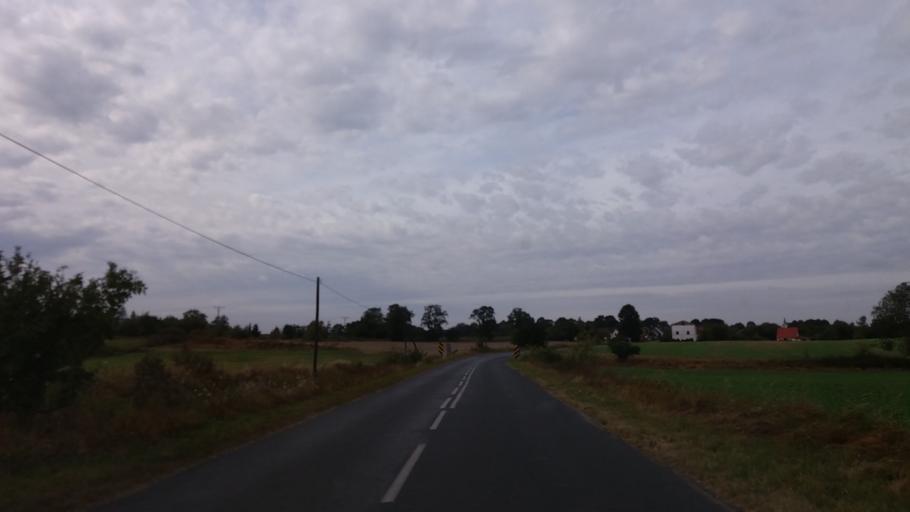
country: PL
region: Lubusz
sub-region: Powiat strzelecko-drezdenecki
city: Strzelce Krajenskie
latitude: 52.9195
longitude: 15.4873
